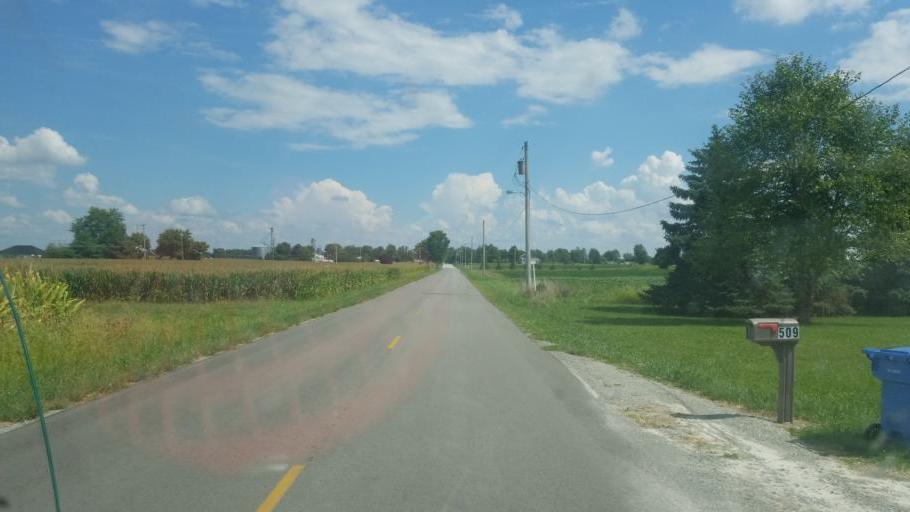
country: US
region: Ohio
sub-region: Hardin County
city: Forest
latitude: 40.8612
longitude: -83.4748
